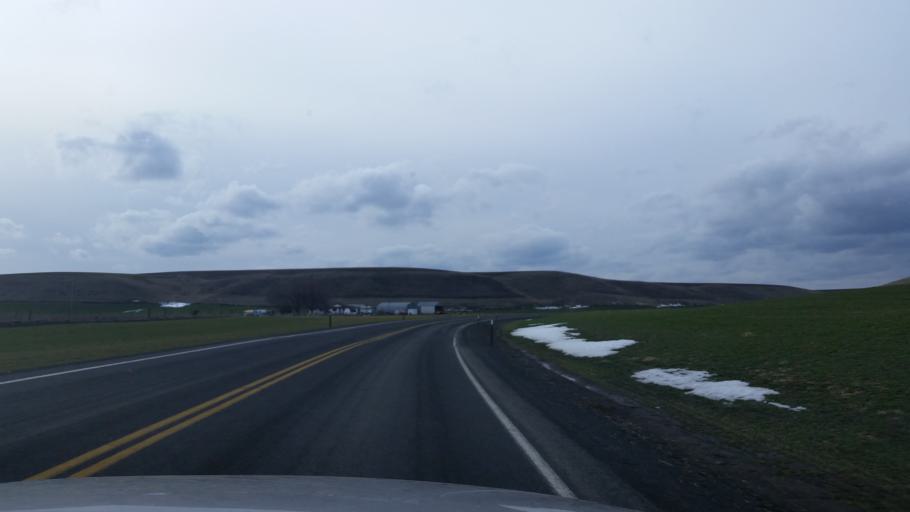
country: US
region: Washington
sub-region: Spokane County
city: Cheney
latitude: 47.1111
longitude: -117.8177
